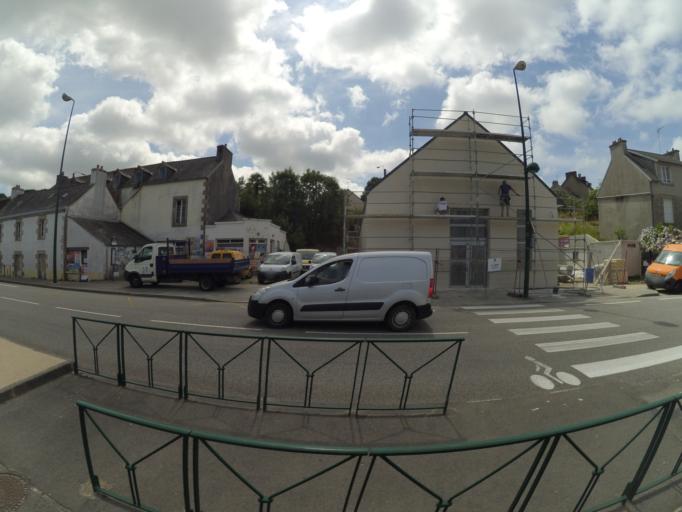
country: FR
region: Brittany
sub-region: Departement du Finistere
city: Quimper
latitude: 47.9912
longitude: -4.0747
